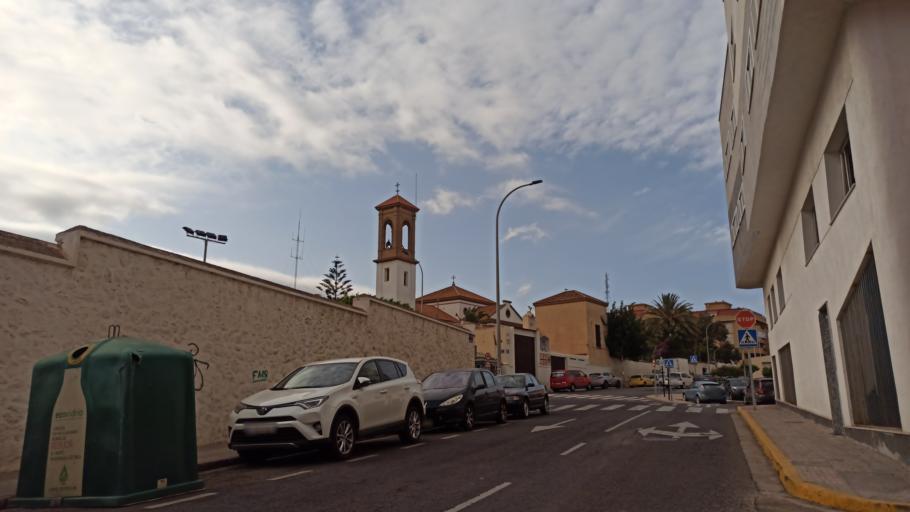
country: ES
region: Melilla
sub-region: Melilla
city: Melilla
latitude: 35.2856
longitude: -2.9481
